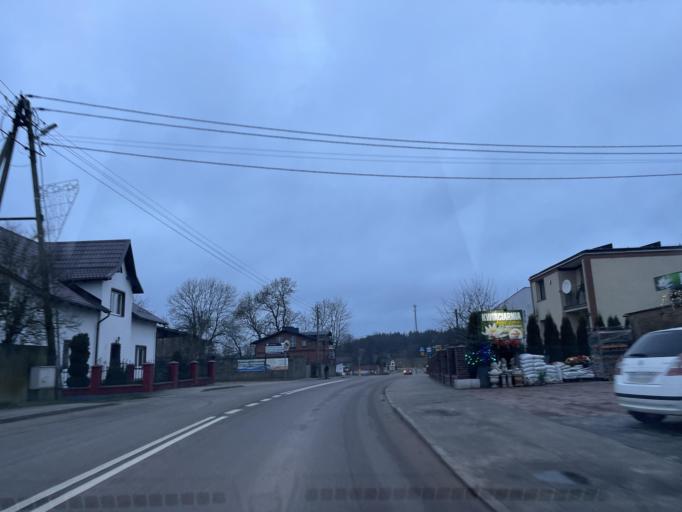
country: PL
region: Pomeranian Voivodeship
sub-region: Powiat wejherowski
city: Szemud
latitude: 54.4149
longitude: 18.2009
